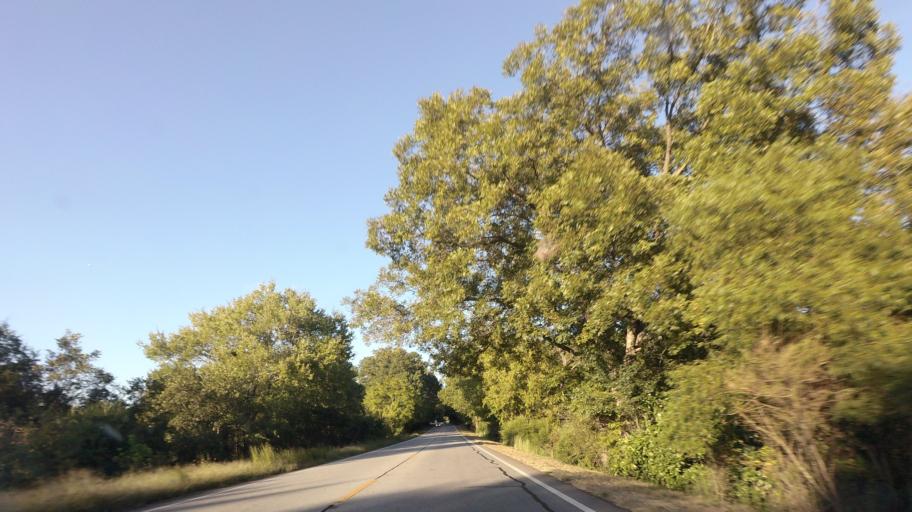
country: US
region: Georgia
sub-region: Spalding County
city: East Griffin
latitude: 33.2693
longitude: -84.2106
